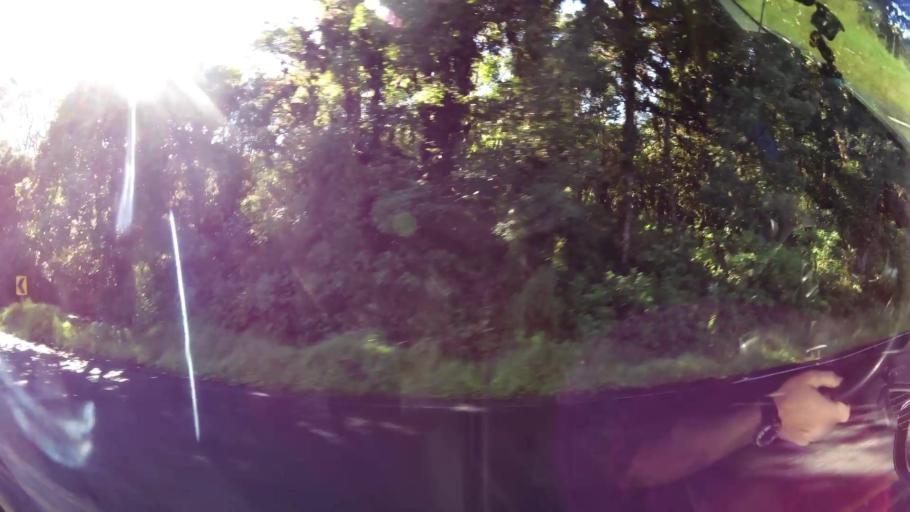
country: CR
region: San Jose
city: San Marcos
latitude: 9.7137
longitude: -83.9498
